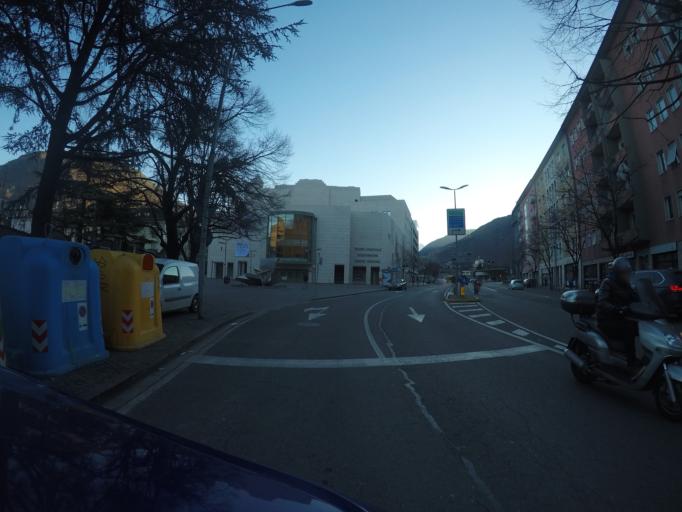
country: IT
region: Trentino-Alto Adige
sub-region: Bolzano
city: Bolzano
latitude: 46.4955
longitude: 11.3527
